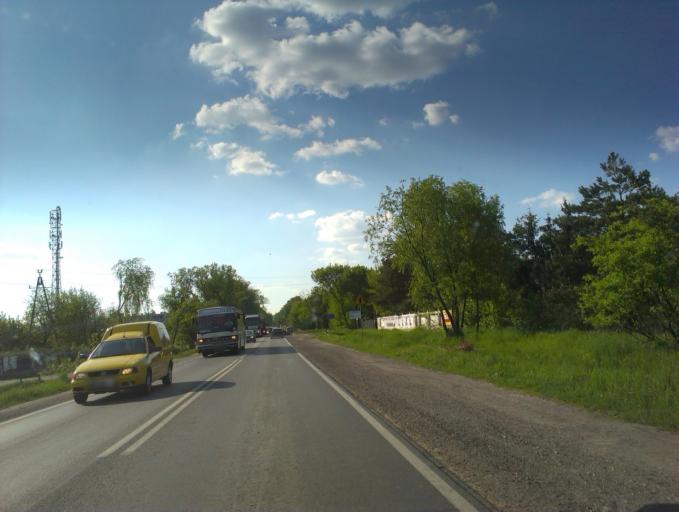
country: PL
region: Masovian Voivodeship
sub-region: Powiat piaseczynski
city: Zabieniec
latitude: 52.0620
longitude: 21.0404
